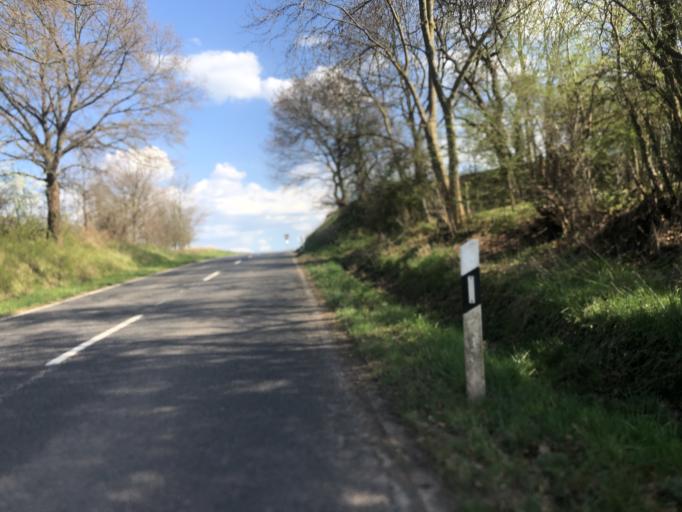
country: DE
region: North Rhine-Westphalia
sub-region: Regierungsbezirk Koln
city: Kall
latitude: 50.5886
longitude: 6.5747
